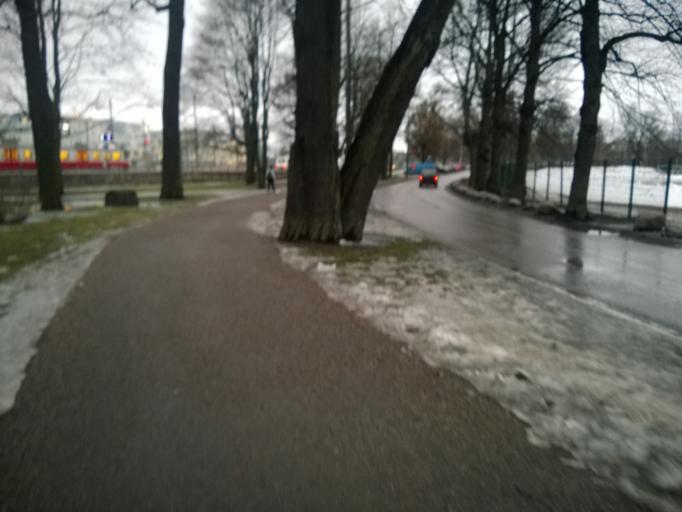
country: FI
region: Uusimaa
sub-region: Helsinki
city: Helsinki
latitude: 60.1741
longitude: 24.9428
